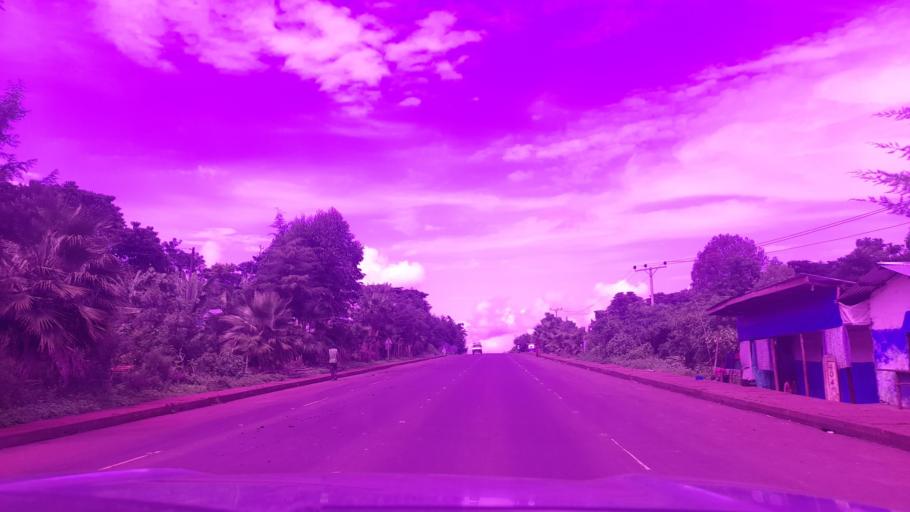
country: ET
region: Oromiya
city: Jima
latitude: 7.5135
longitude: 36.5263
